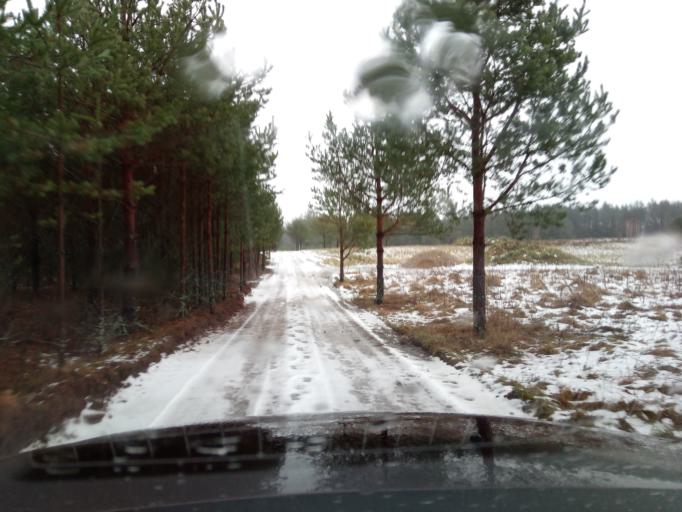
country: LT
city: Svencioneliai
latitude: 55.3353
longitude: 25.8041
